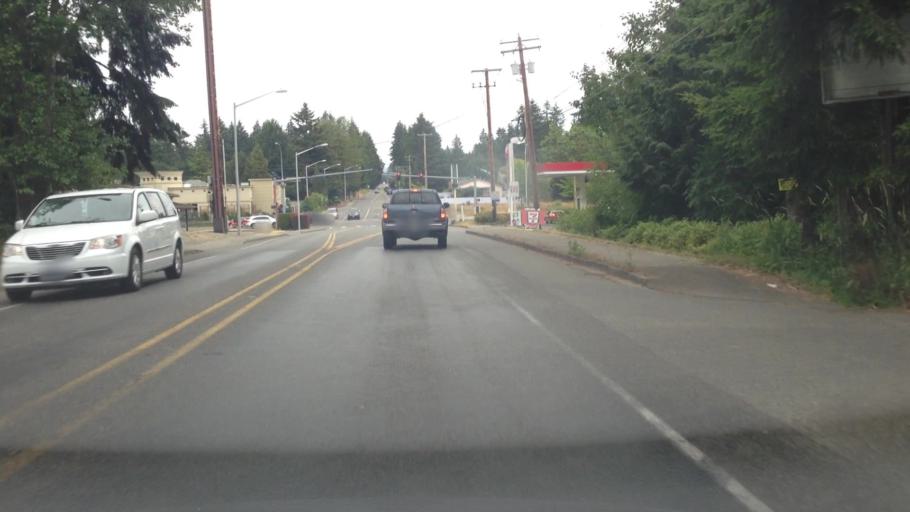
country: US
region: Washington
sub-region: Pierce County
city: South Hill
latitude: 47.1184
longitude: -122.2952
